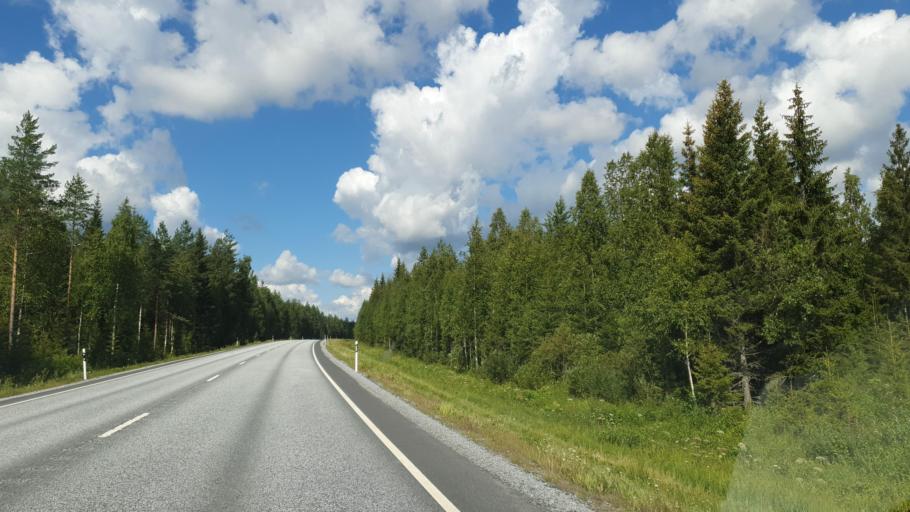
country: FI
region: Northern Savo
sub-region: Ylae-Savo
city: Sonkajaervi
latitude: 63.9005
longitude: 27.3976
